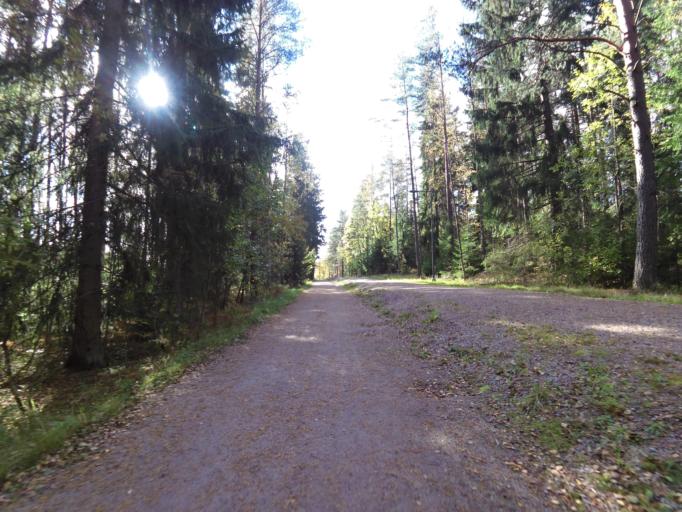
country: FI
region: Uusimaa
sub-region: Helsinki
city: Kauniainen
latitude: 60.1789
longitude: 24.6981
